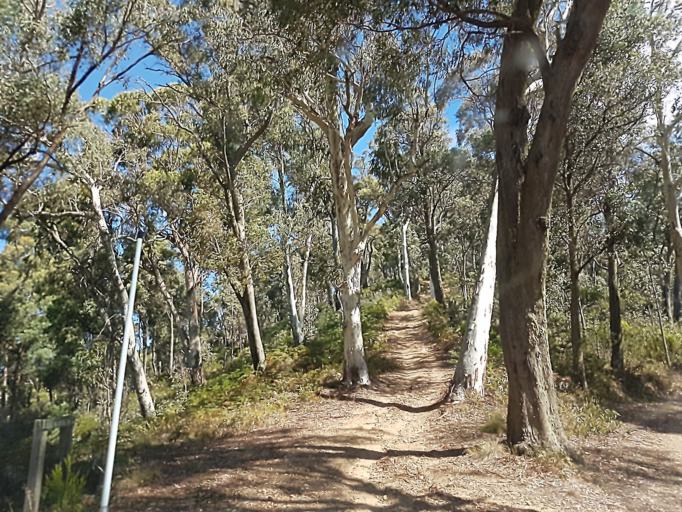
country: AU
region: Victoria
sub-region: Alpine
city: Mount Beauty
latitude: -36.8789
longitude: 147.0263
